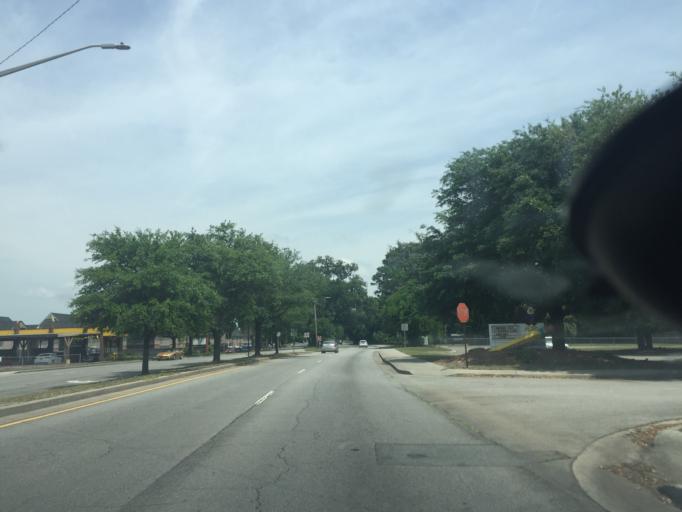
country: US
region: Georgia
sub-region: Chatham County
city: Montgomery
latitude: 31.9914
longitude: -81.1277
